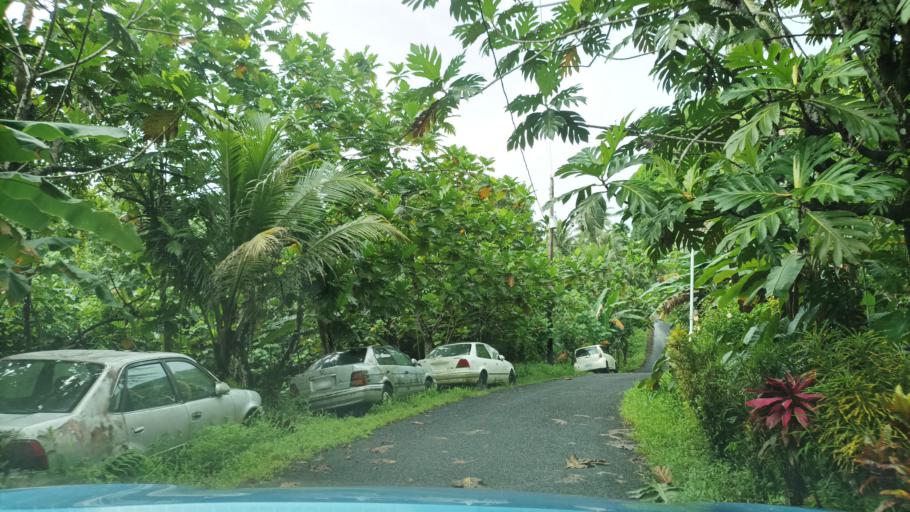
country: FM
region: Pohnpei
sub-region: Kolonia Municipality
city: Kolonia
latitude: 6.9181
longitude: 158.2753
